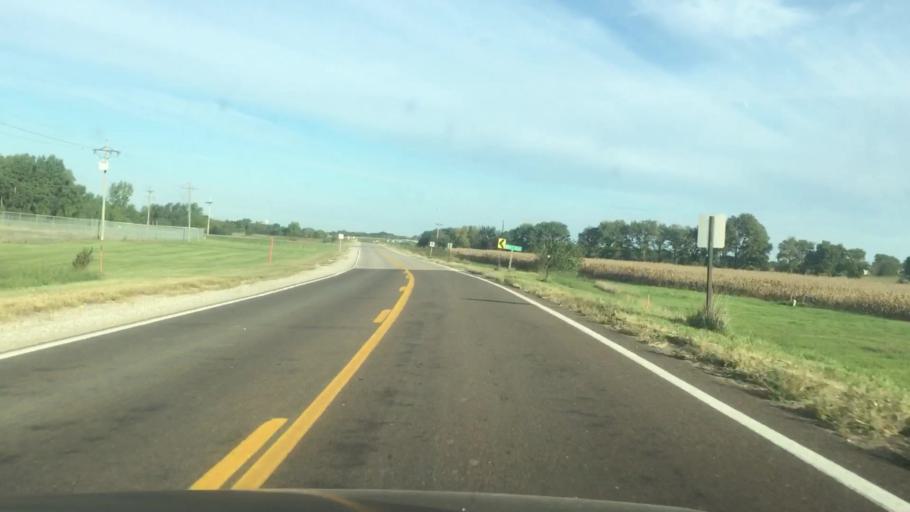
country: US
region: Nebraska
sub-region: Jefferson County
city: Fairbury
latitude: 40.1227
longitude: -97.1593
